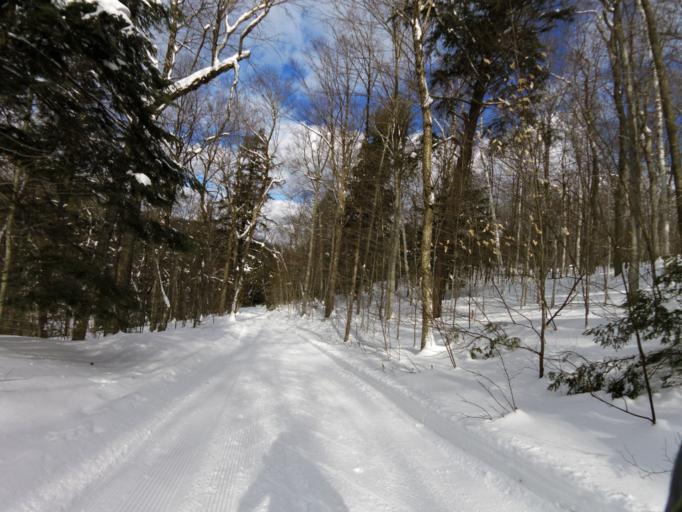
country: CA
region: Quebec
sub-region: Outaouais
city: Wakefield
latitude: 45.5328
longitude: -75.8669
